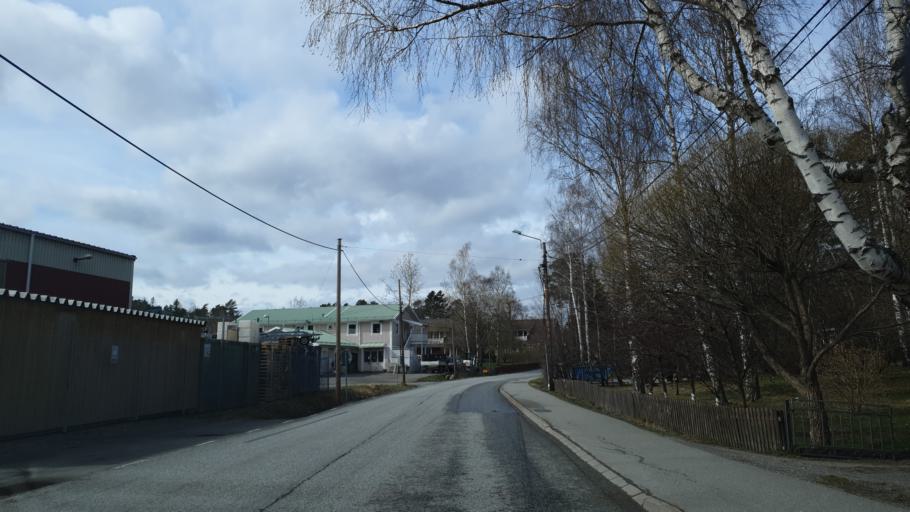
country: SE
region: Stockholm
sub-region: Nacka Kommun
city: Boo
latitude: 59.3234
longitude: 18.2928
